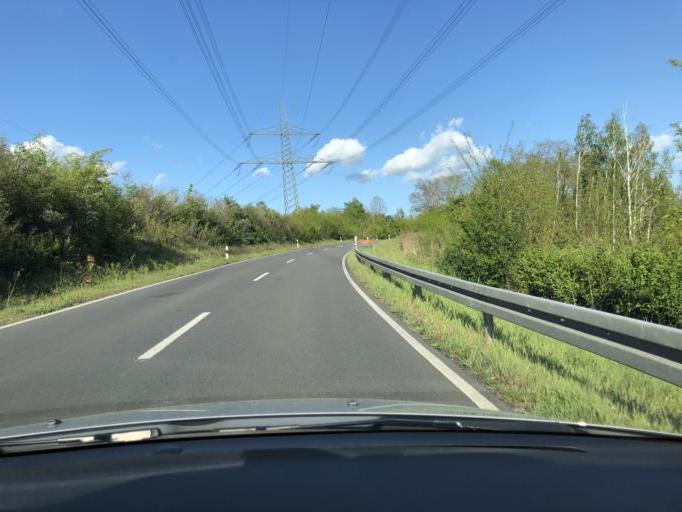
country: DE
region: Saxony
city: Rotha
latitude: 51.1847
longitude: 12.4226
